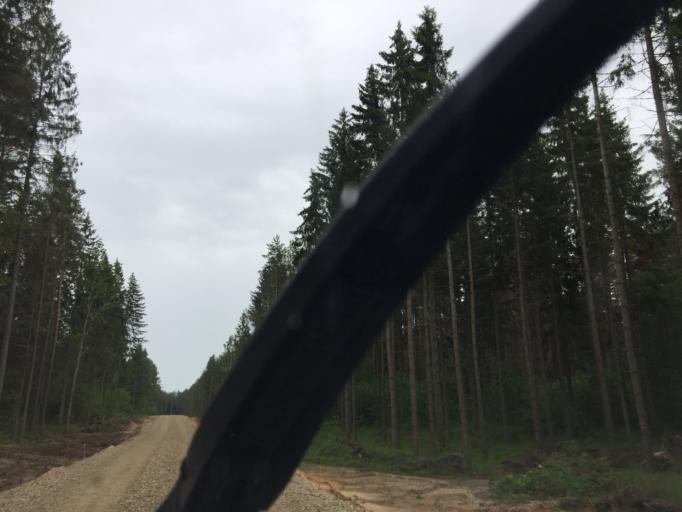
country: LV
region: Tukuma Rajons
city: Tukums
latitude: 57.0060
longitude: 23.1014
